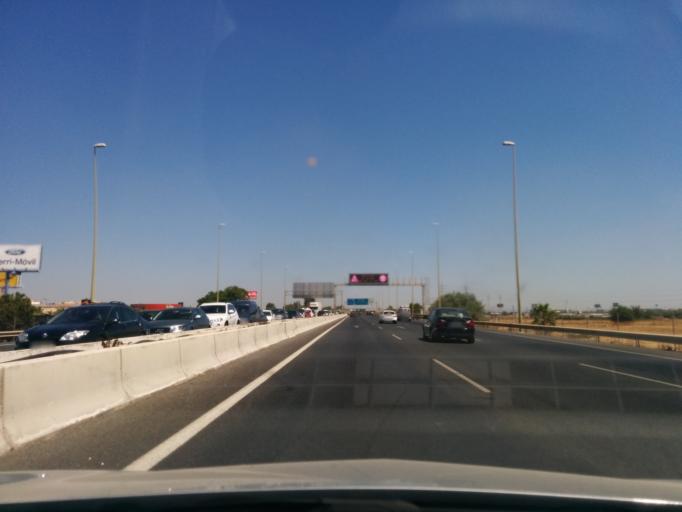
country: ES
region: Andalusia
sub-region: Provincia de Sevilla
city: Tomares
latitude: 37.3805
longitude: -6.0261
